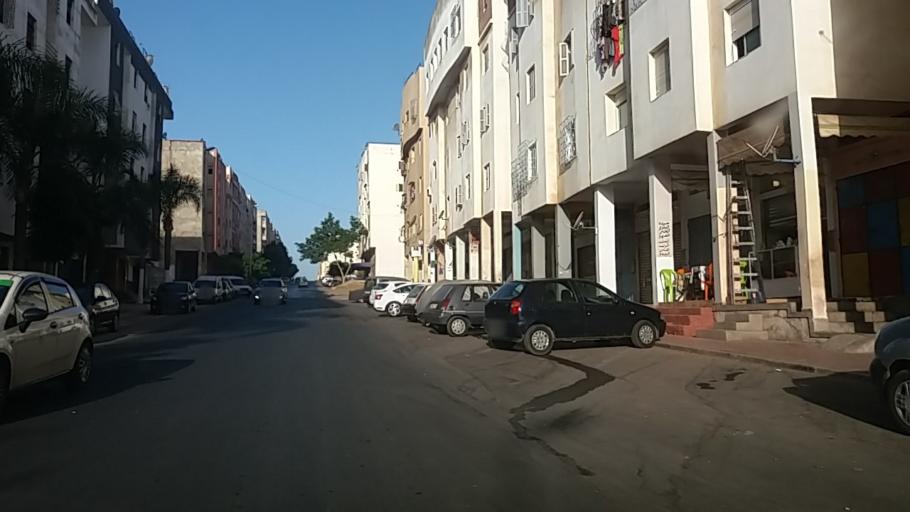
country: MA
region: Gharb-Chrarda-Beni Hssen
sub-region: Kenitra Province
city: Kenitra
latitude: 34.2573
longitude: -6.6163
